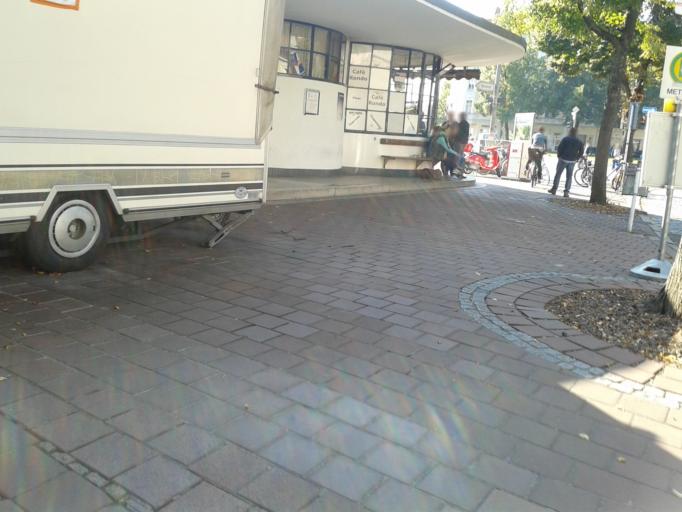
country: DE
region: Bavaria
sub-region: Upper Franconia
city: Bamberg
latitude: 49.8922
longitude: 10.8924
